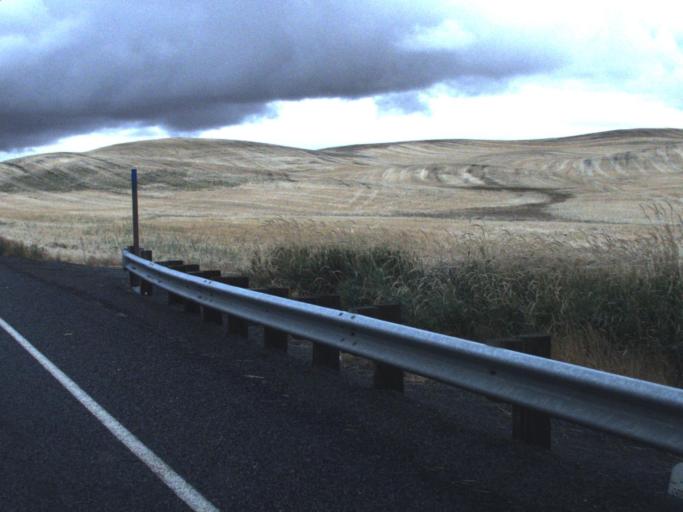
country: US
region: Washington
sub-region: Whitman County
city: Colfax
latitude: 47.1848
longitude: -117.3066
